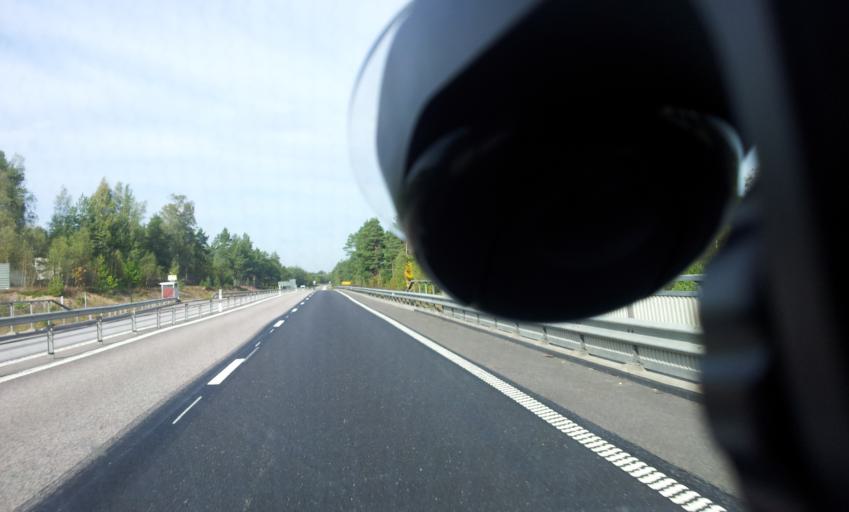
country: SE
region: Kalmar
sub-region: Oskarshamns Kommun
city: Oskarshamn
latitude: 57.3827
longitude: 16.4817
